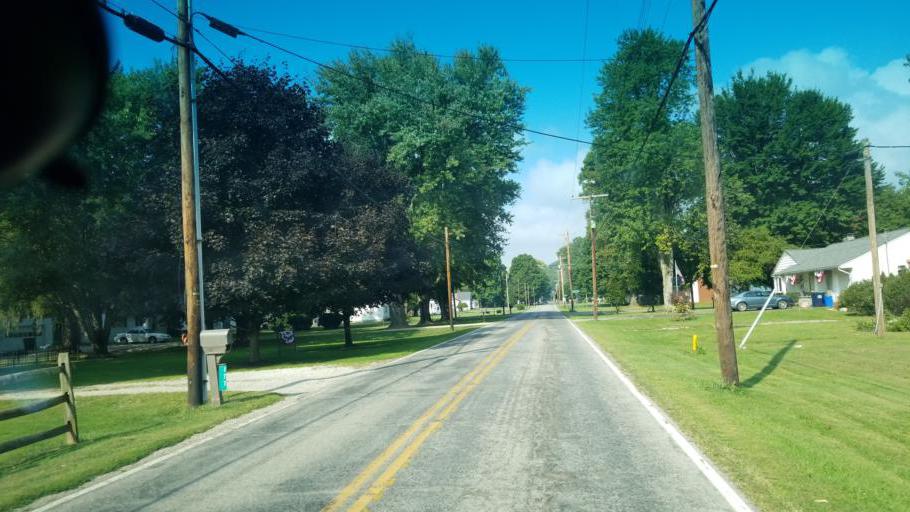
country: US
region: Ohio
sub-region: Licking County
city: Newark
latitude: 40.1167
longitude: -82.4356
